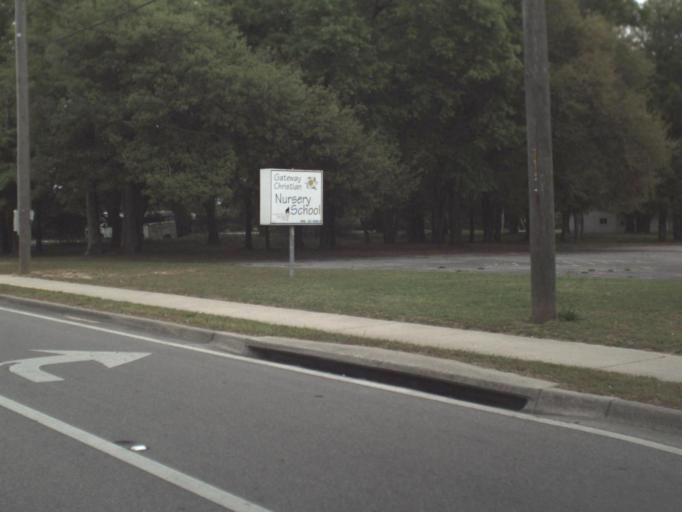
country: US
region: Florida
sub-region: Escambia County
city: Brent
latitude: 30.4708
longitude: -87.2317
